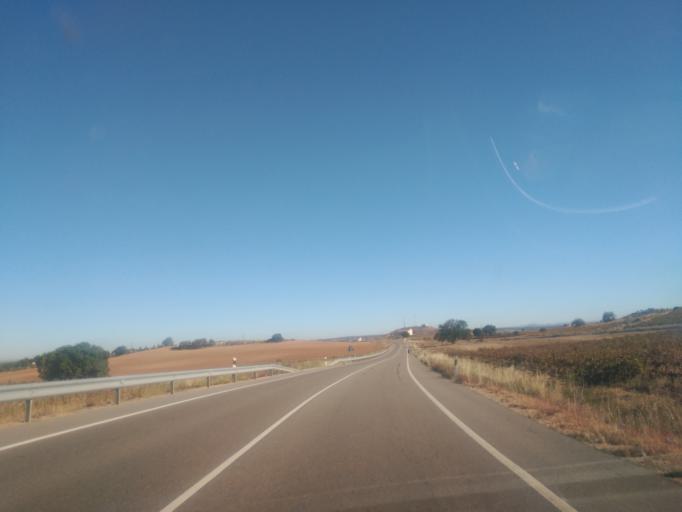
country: ES
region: Castille and Leon
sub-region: Provincia de Burgos
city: Castrillo de la Vega
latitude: 41.6389
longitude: -3.7814
